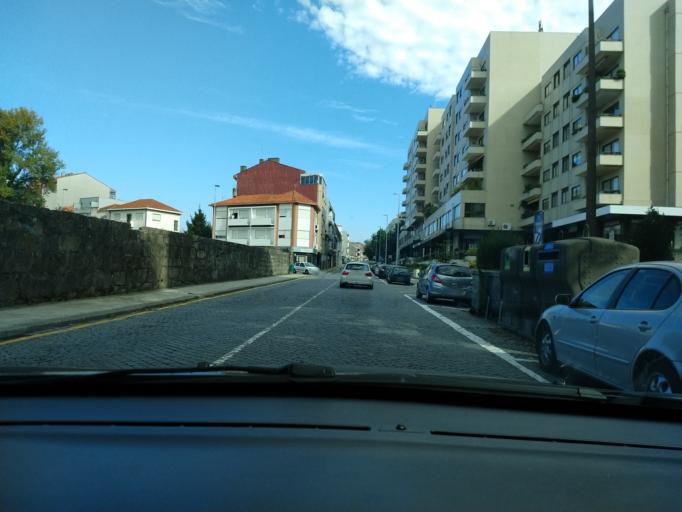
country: PT
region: Porto
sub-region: Porto
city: Porto
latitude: 41.1627
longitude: -8.5998
